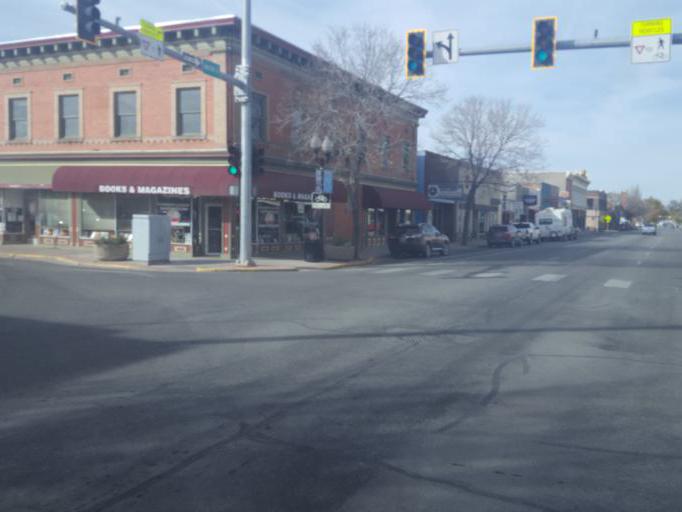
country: US
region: Colorado
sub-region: Alamosa County
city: Alamosa
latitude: 37.4683
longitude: -105.8651
